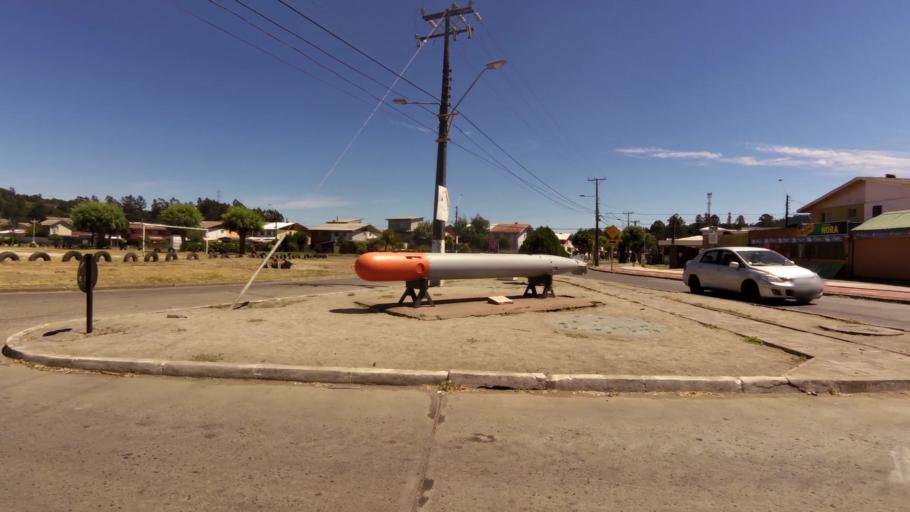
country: CL
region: Biobio
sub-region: Provincia de Concepcion
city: Talcahuano
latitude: -36.7616
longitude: -73.0933
